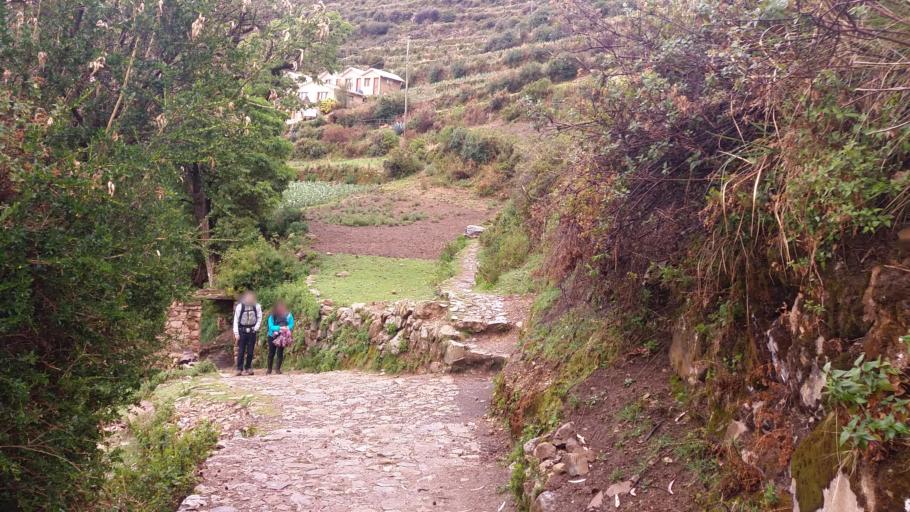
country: BO
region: La Paz
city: Yumani
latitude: -16.0383
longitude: -69.1456
